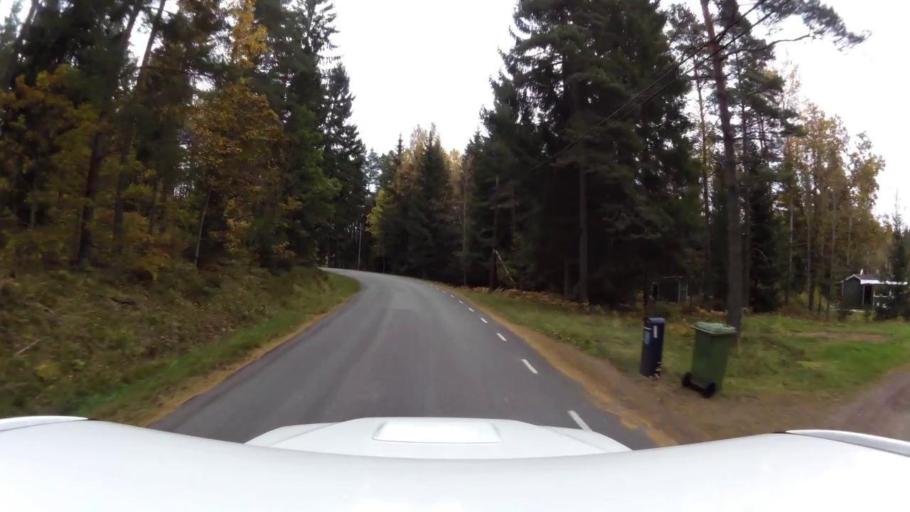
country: SE
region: OEstergoetland
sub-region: Linkopings Kommun
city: Ljungsbro
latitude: 58.5440
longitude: 15.4153
